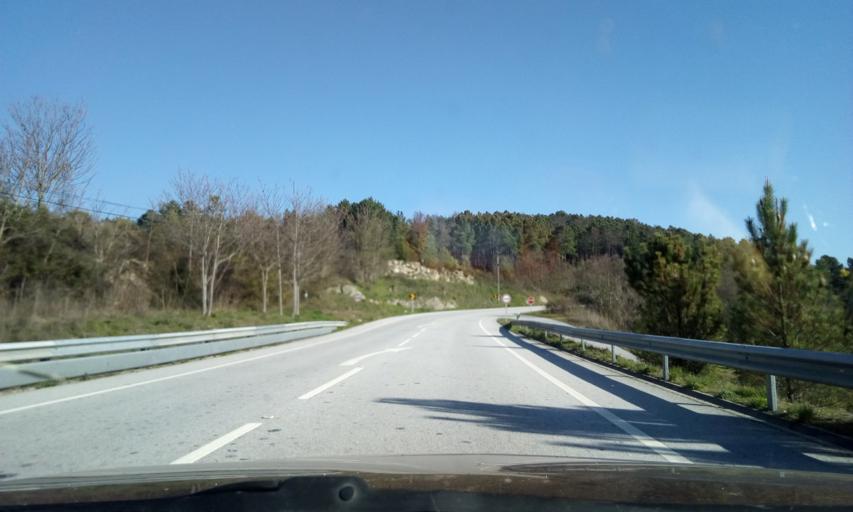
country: PT
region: Guarda
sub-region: Fornos de Algodres
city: Fornos de Algodres
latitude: 40.6202
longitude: -7.5114
